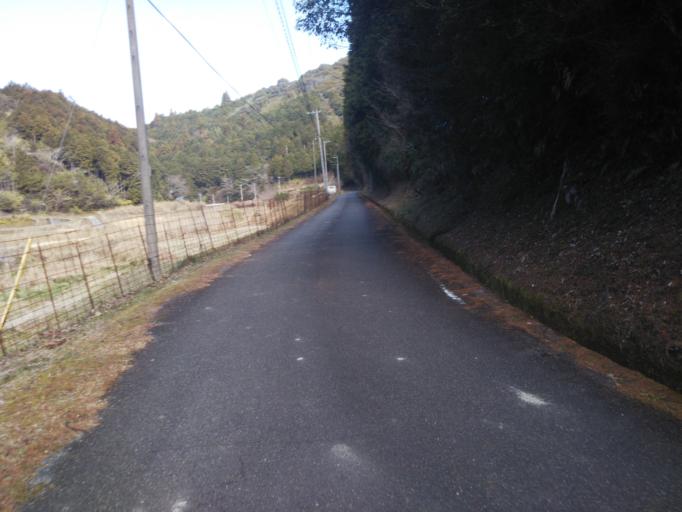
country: JP
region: Kochi
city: Nakamura
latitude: 33.0380
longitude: 132.9851
